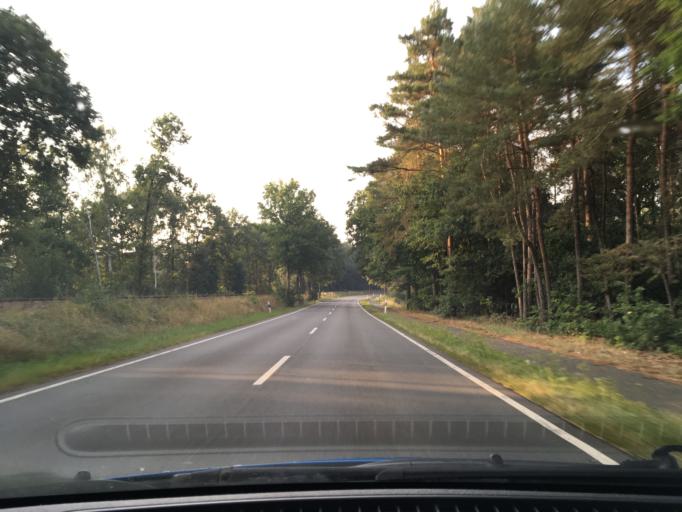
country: DE
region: Lower Saxony
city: Celle
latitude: 52.6883
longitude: 10.0754
